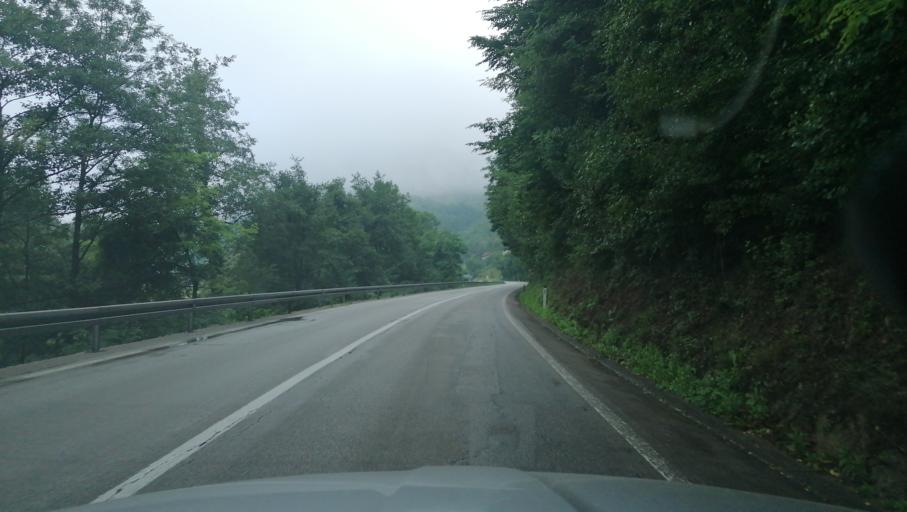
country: BA
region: Federation of Bosnia and Herzegovina
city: Donji Vakuf
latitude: 44.1693
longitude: 17.3604
